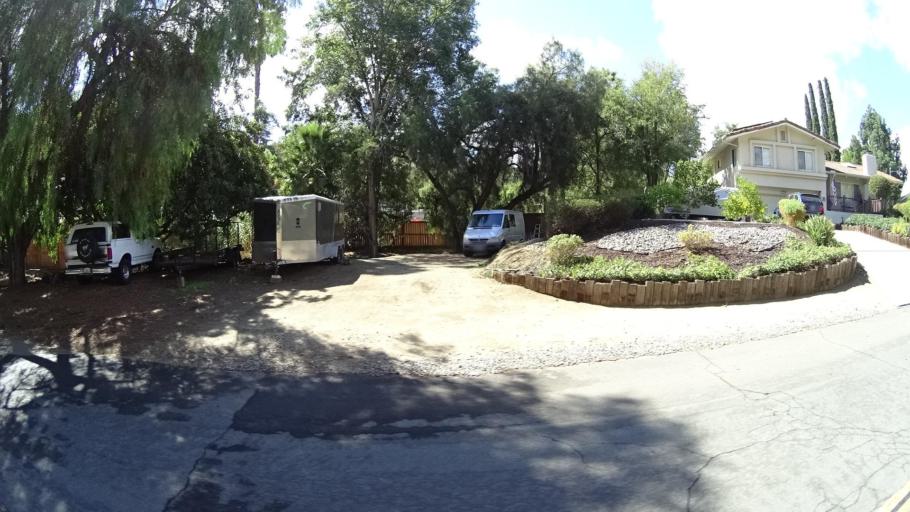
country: US
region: California
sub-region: San Diego County
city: Rancho San Diego
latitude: 32.7599
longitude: -116.9498
